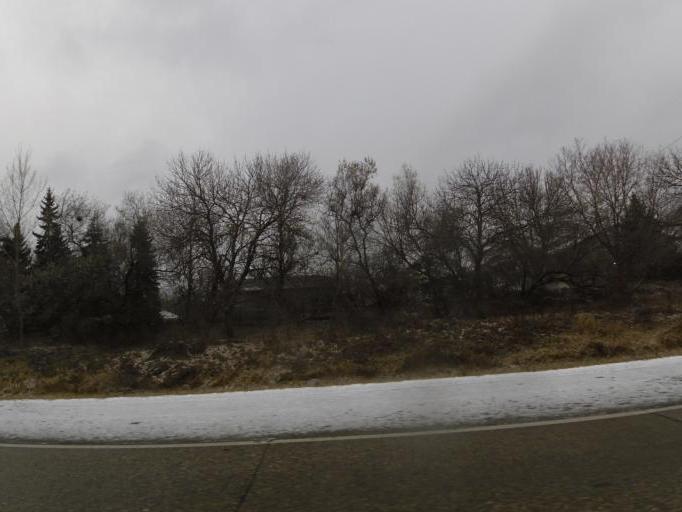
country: US
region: Minnesota
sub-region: Dakota County
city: Eagan
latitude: 44.7968
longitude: -93.2222
